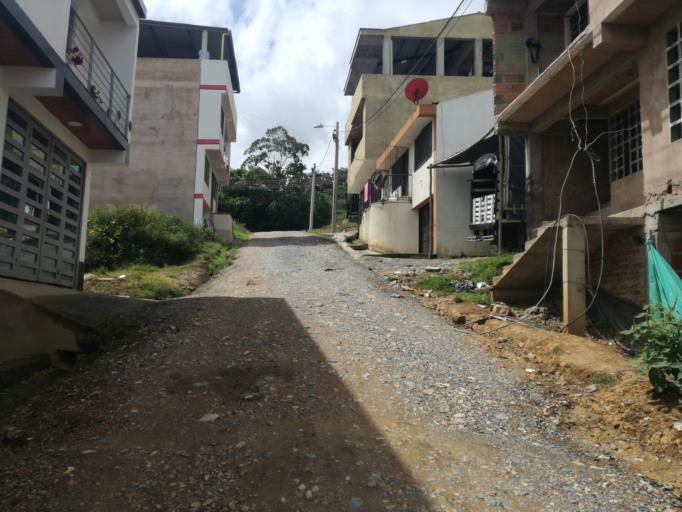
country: CO
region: Boyaca
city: Santana
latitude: 6.0561
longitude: -73.4846
